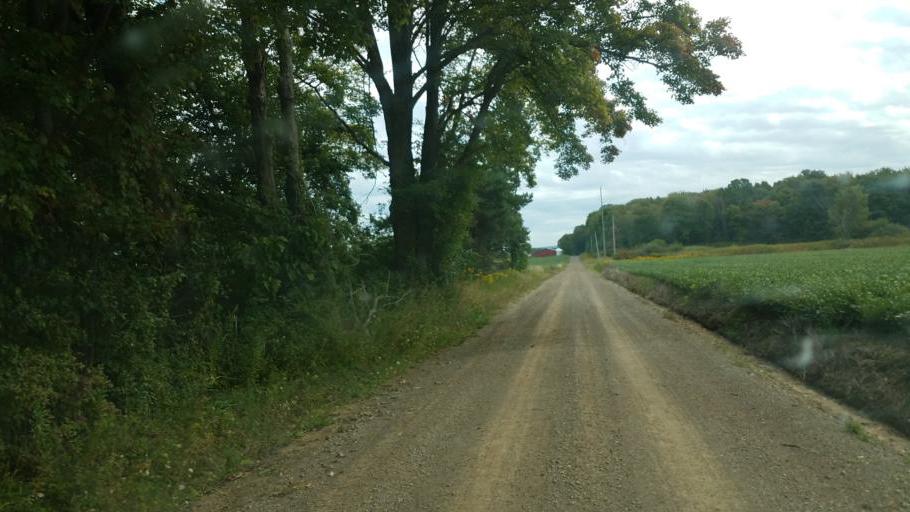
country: US
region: Pennsylvania
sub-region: Crawford County
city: Pymatuning Central
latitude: 41.5265
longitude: -80.4073
